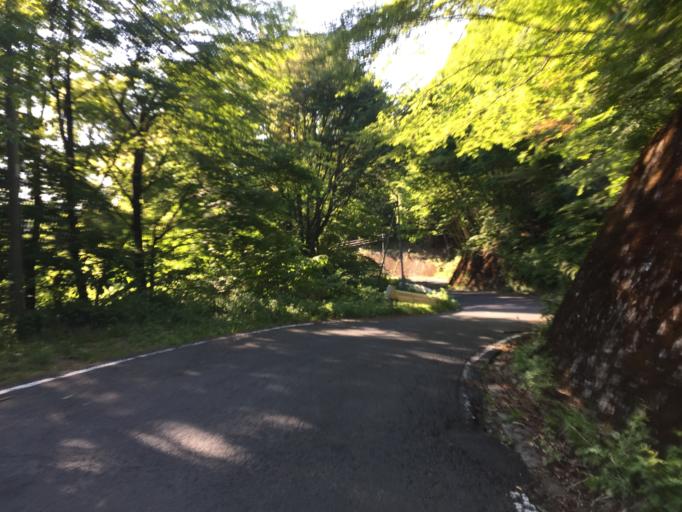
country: JP
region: Ibaraki
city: Kitaibaraki
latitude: 36.9113
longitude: 140.5823
